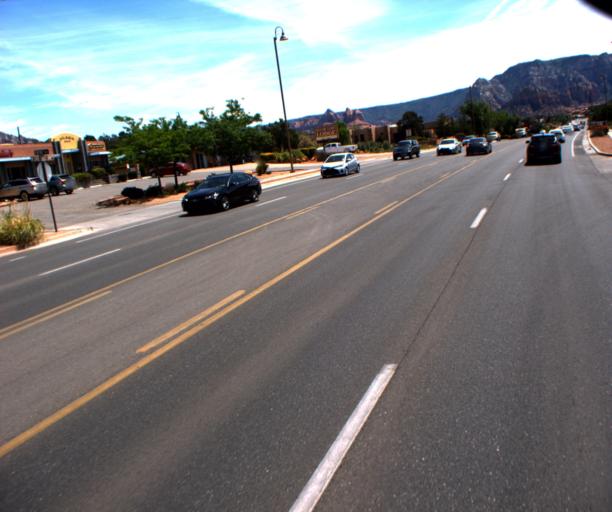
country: US
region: Arizona
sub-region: Yavapai County
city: West Sedona
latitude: 34.8639
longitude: -111.7936
